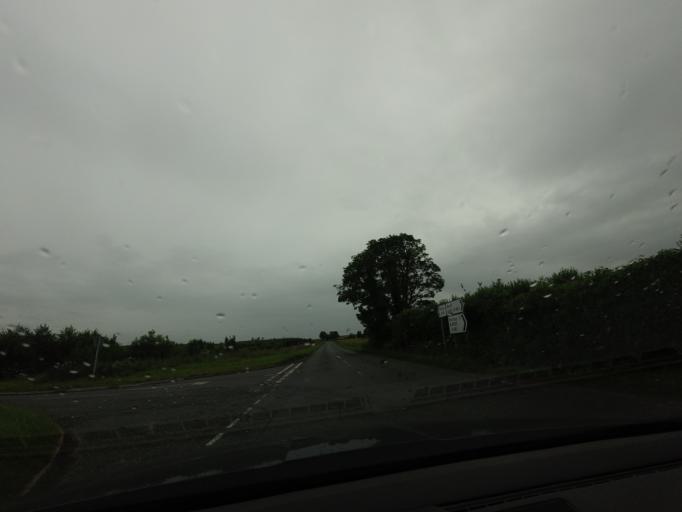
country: GB
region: Scotland
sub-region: Aberdeenshire
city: Portsoy
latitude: 57.6411
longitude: -2.6506
